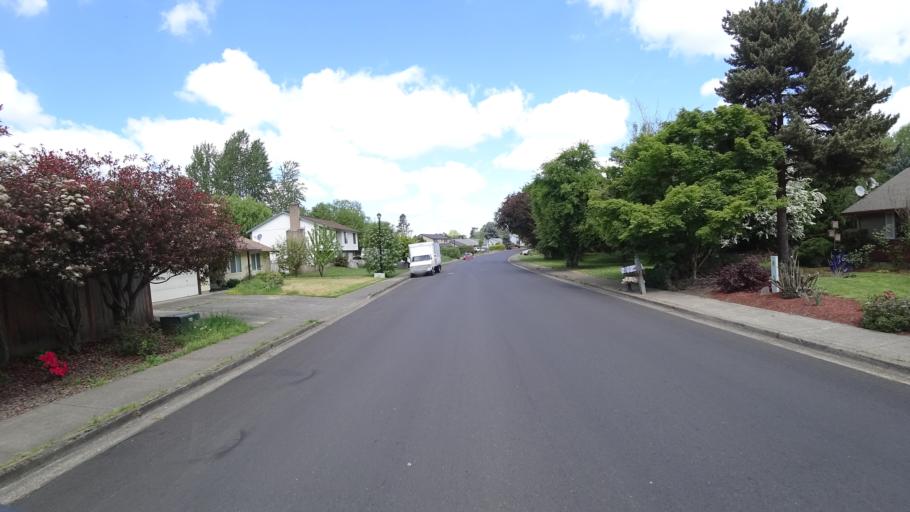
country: US
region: Oregon
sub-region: Washington County
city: Aloha
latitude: 45.5044
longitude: -122.8941
